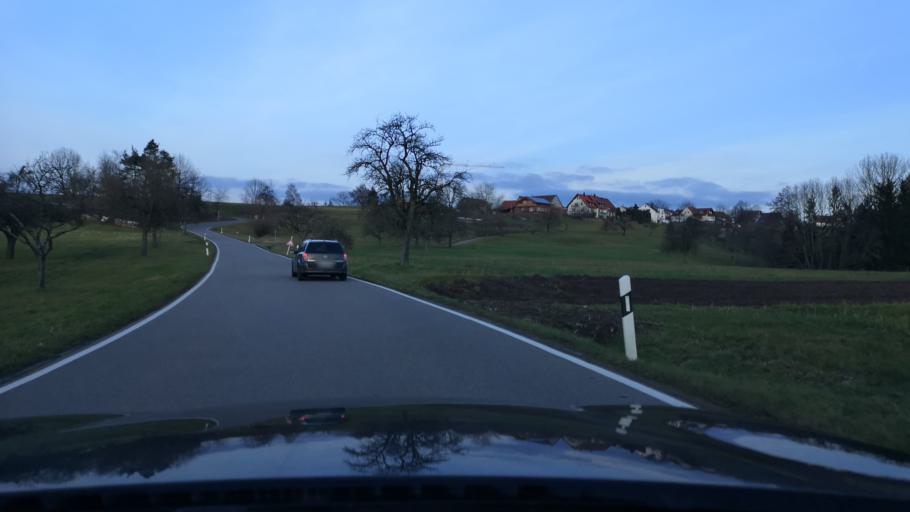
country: DE
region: Baden-Wuerttemberg
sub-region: Regierungsbezirk Stuttgart
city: Rudersberg
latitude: 48.9053
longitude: 9.5280
